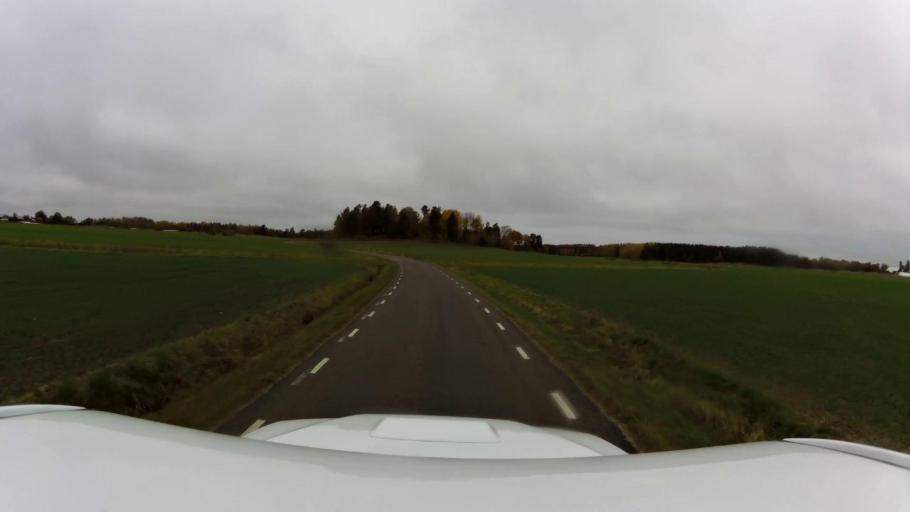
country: SE
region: OEstergoetland
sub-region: Linkopings Kommun
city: Linghem
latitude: 58.4861
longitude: 15.8106
